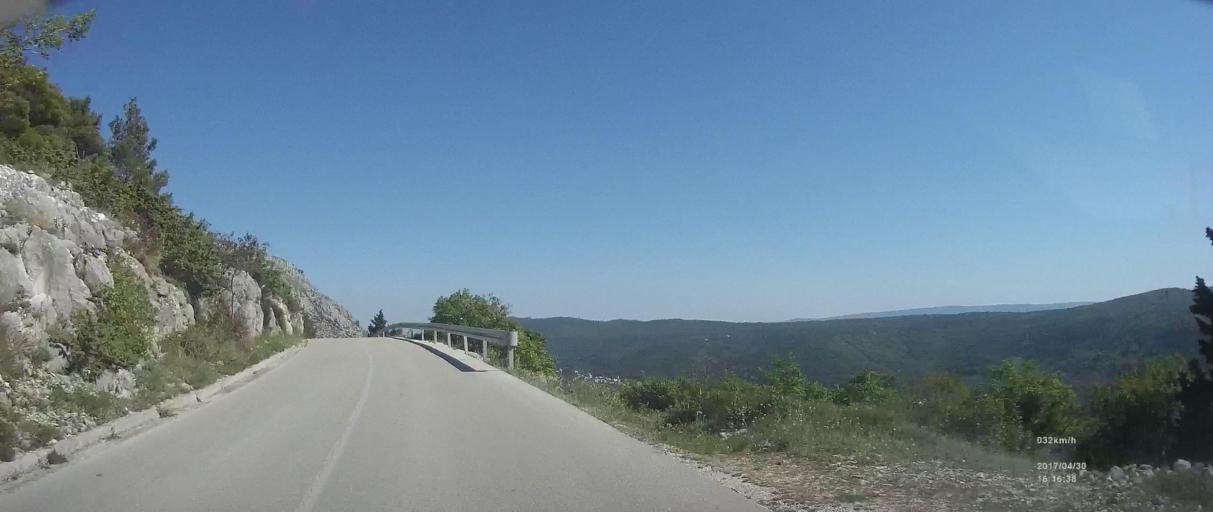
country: HR
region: Splitsko-Dalmatinska
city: Srinjine
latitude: 43.5018
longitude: 16.6060
